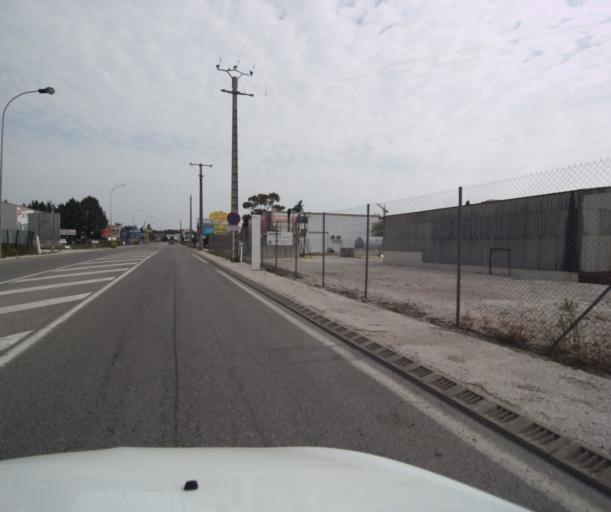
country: FR
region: Provence-Alpes-Cote d'Azur
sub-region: Departement du Var
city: La Farlede
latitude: 43.1430
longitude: 6.0375
